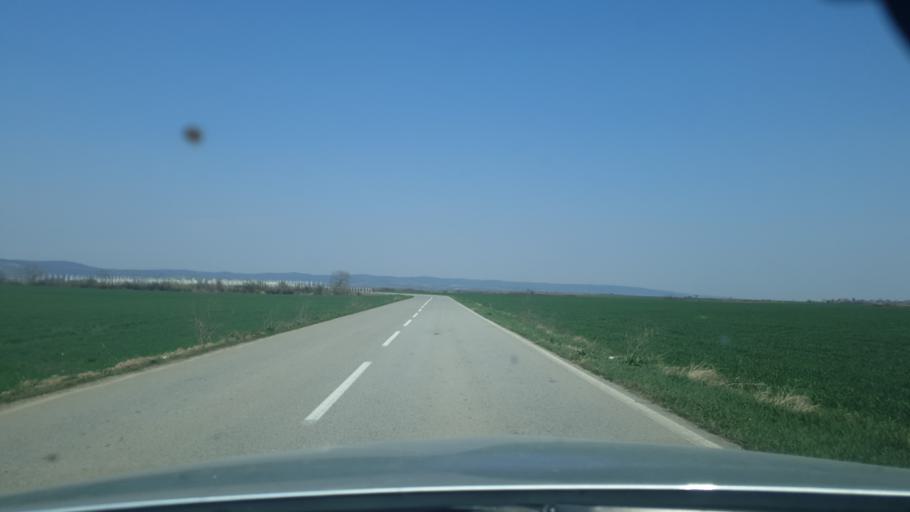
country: RS
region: Autonomna Pokrajina Vojvodina
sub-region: Sremski Okrug
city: Ruma
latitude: 45.0479
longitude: 19.7636
